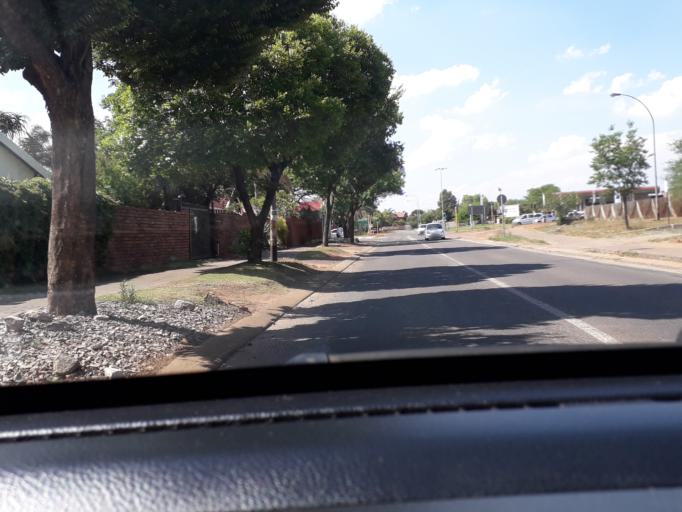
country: ZA
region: Gauteng
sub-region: City of Tshwane Metropolitan Municipality
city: Centurion
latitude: -25.8400
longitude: 28.2389
